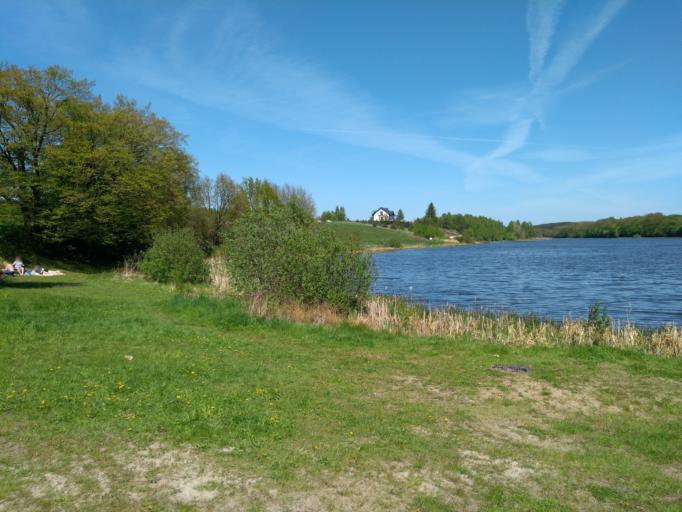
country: PL
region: Pomeranian Voivodeship
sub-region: Powiat kartuski
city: Chwaszczyno
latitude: 54.4191
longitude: 18.4425
